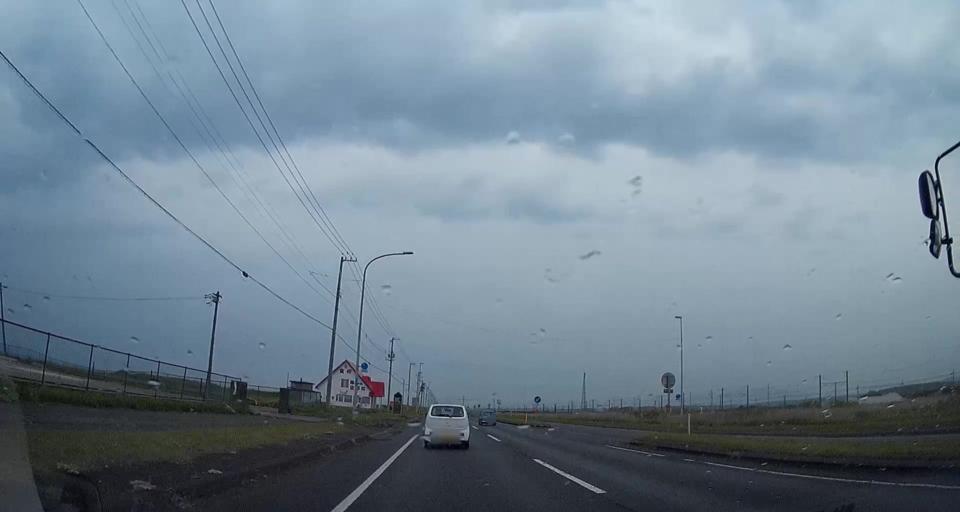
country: JP
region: Hokkaido
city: Shiraoi
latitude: 42.5969
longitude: 141.4731
